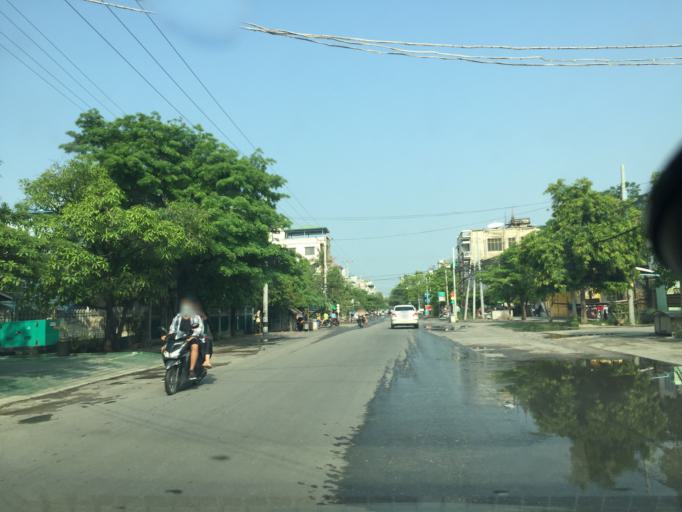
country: MM
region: Mandalay
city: Mandalay
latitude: 21.9732
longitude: 96.0972
